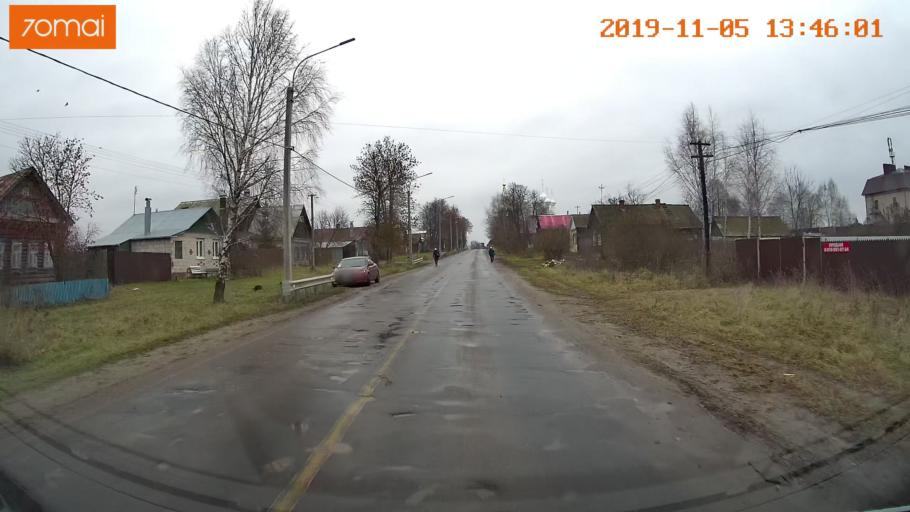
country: RU
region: Ivanovo
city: Shuya
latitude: 56.9930
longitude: 41.4102
